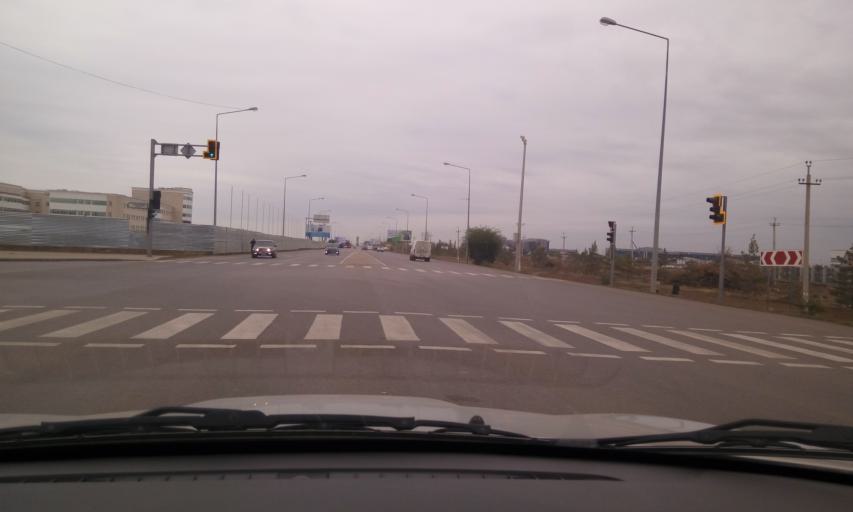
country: KZ
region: Astana Qalasy
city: Astana
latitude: 51.0866
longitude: 71.4016
